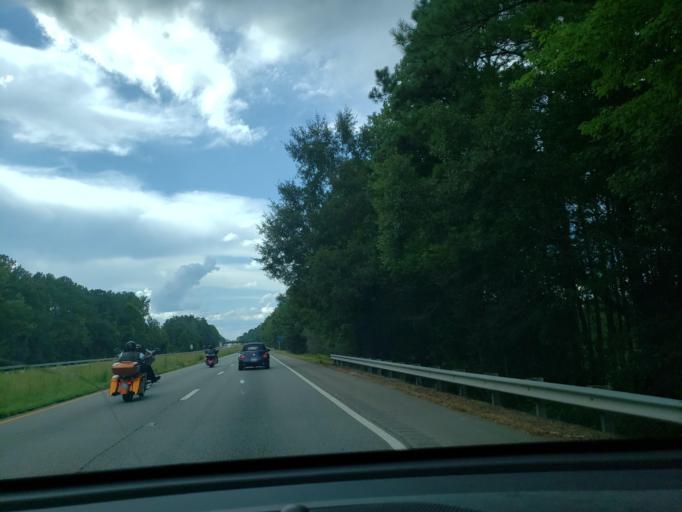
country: US
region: Virginia
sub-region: City of Franklin
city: Franklin
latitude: 36.6424
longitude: -76.9008
